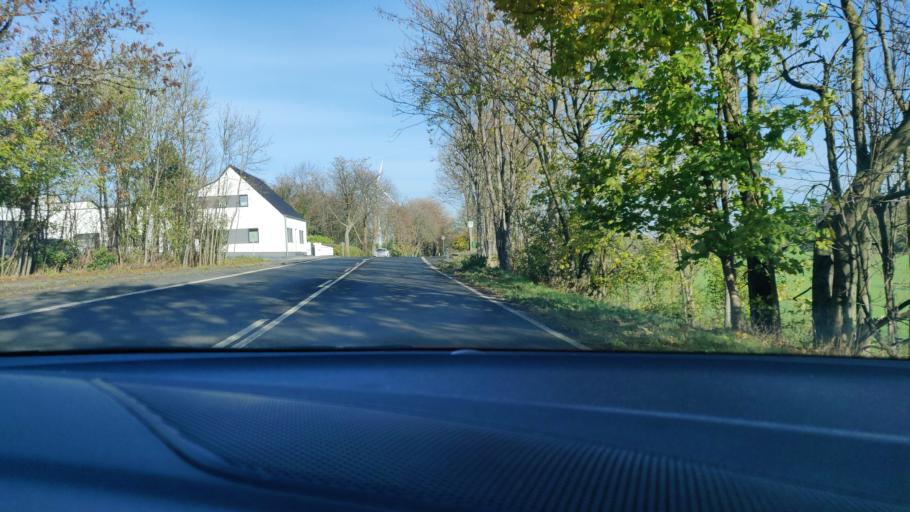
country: DE
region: North Rhine-Westphalia
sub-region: Regierungsbezirk Dusseldorf
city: Velbert
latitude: 51.3562
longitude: 7.0205
